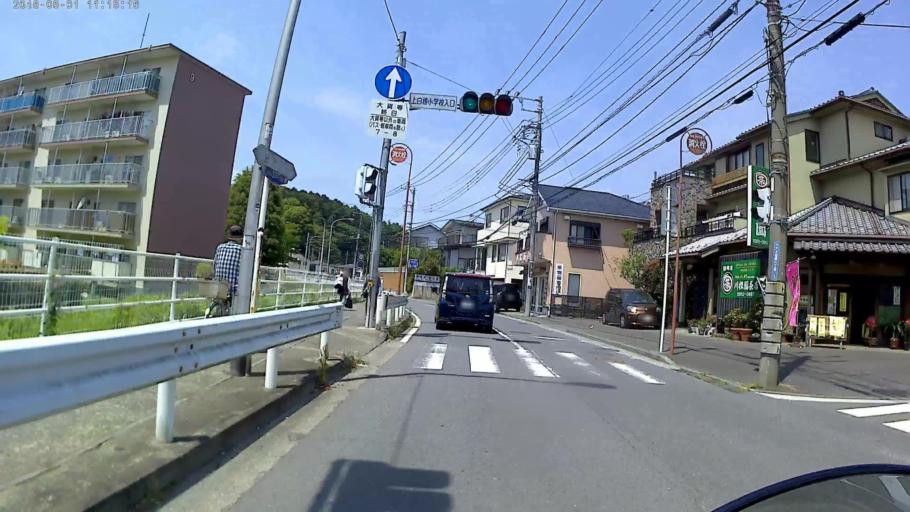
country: JP
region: Kanagawa
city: Minami-rinkan
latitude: 35.4898
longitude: 139.5401
